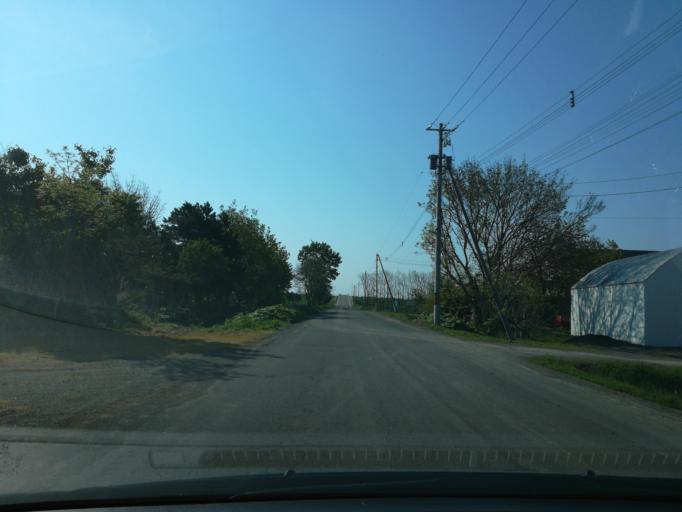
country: JP
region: Hokkaido
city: Ebetsu
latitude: 43.1267
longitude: 141.6207
